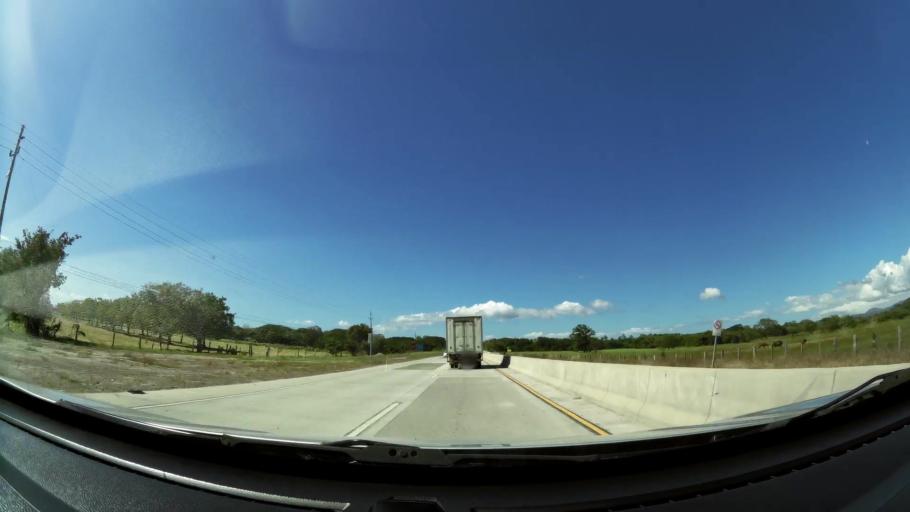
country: CR
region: Guanacaste
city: Liberia
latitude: 10.5858
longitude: -85.4148
